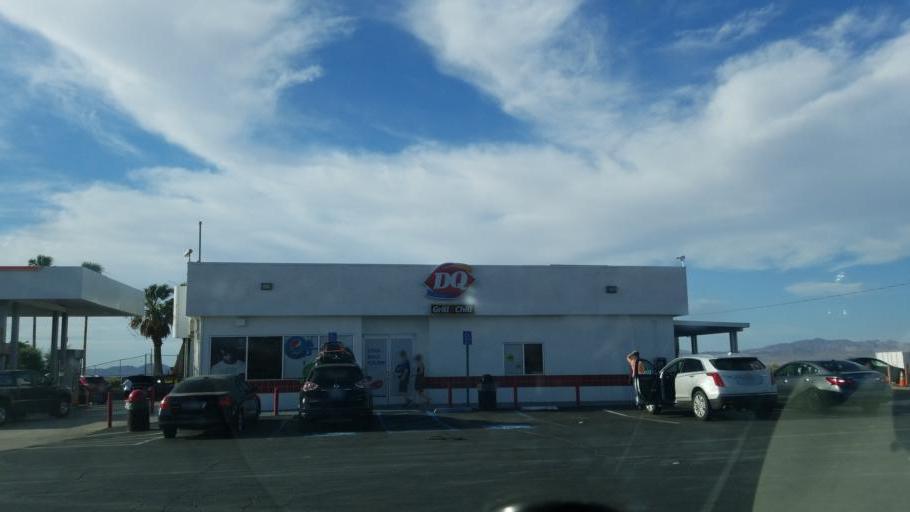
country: US
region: California
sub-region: San Bernardino County
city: Twentynine Palms
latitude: 34.7268
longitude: -116.1627
